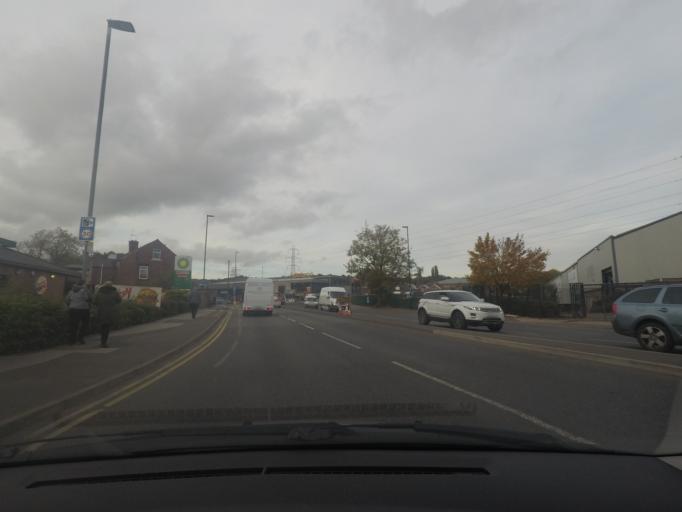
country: GB
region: England
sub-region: Sheffield
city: Oughtibridge
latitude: 53.4152
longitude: -1.5009
